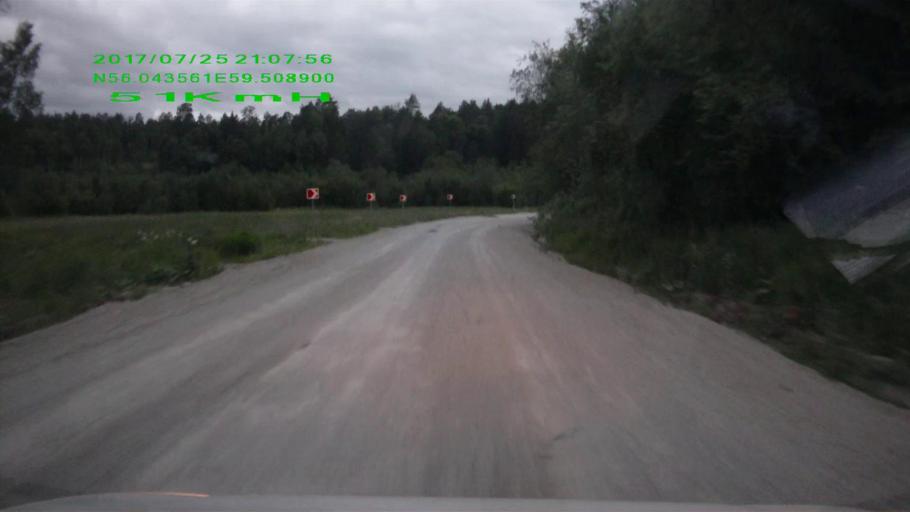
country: RU
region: Chelyabinsk
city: Nyazepetrovsk
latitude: 56.0435
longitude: 59.5084
